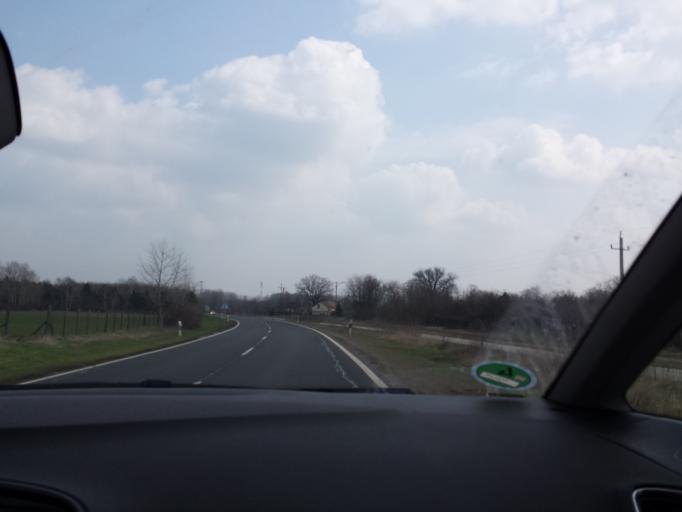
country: HU
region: Bacs-Kiskun
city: Nyarlorinc
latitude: 46.8692
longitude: 19.8578
